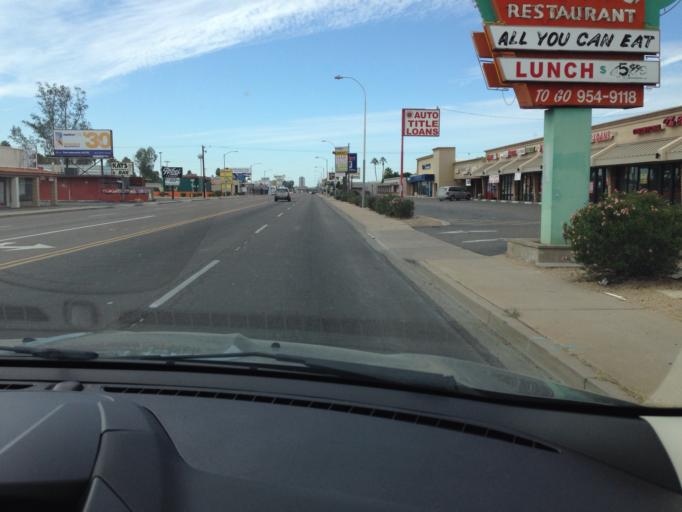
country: US
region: Arizona
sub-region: Maricopa County
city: Phoenix
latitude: 33.4949
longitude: -112.0308
